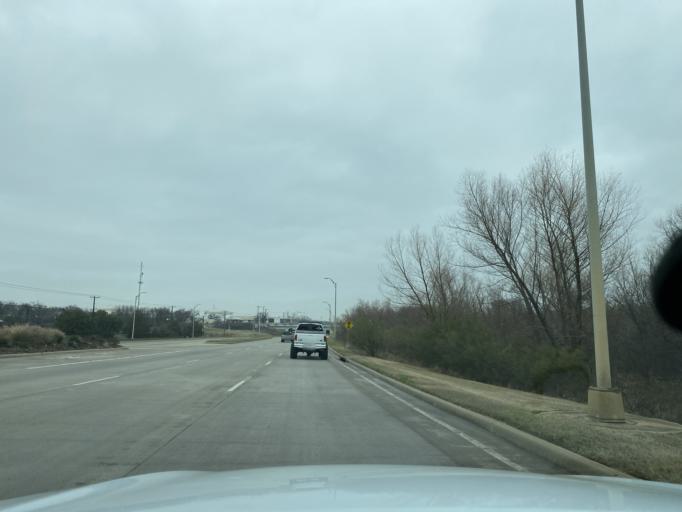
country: US
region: Texas
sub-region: Tarrant County
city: Euless
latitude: 32.8054
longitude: -97.0993
